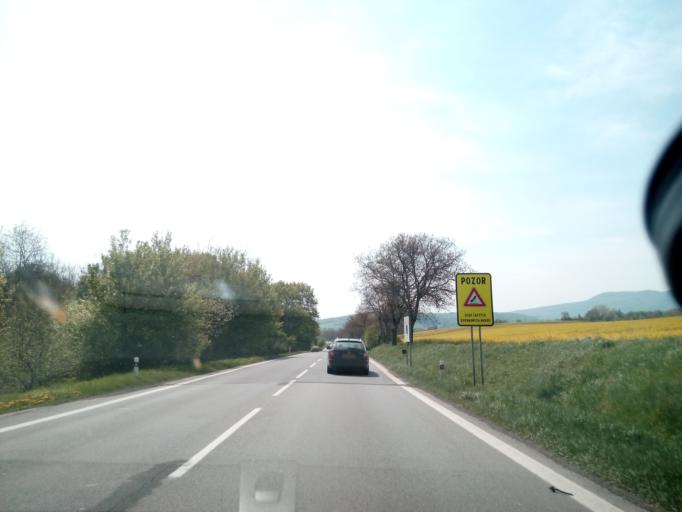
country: SK
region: Presovsky
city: Giraltovce
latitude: 49.0250
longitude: 21.5296
